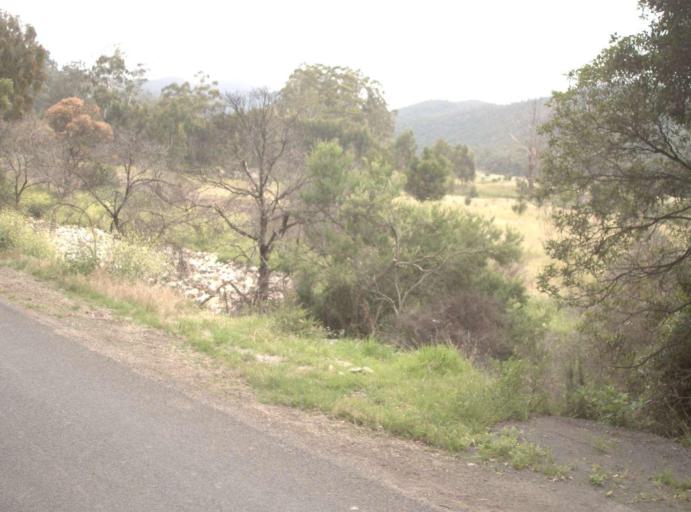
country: AU
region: Victoria
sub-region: Wellington
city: Heyfield
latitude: -37.8038
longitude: 146.6717
